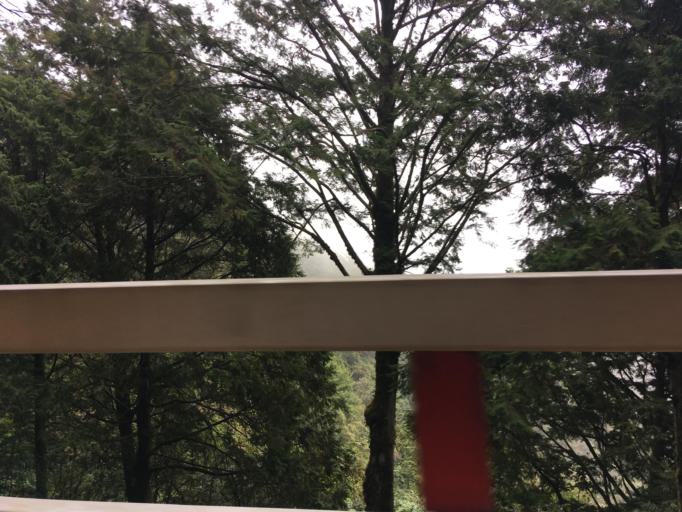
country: TW
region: Taiwan
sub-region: Yilan
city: Yilan
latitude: 24.4852
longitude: 121.5342
